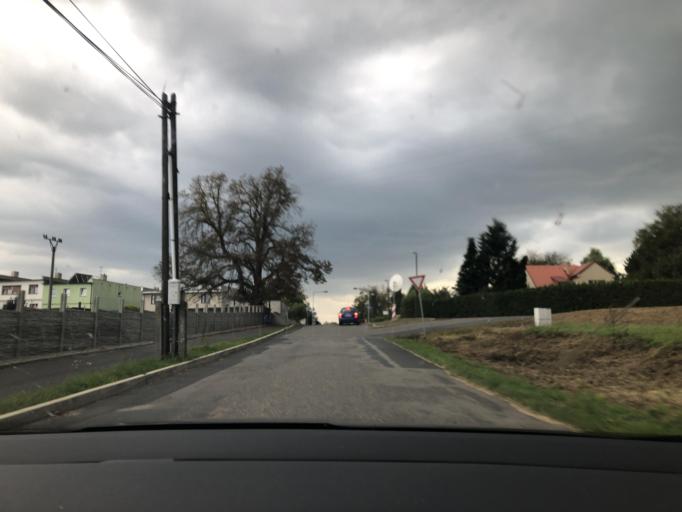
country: CZ
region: Central Bohemia
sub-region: Okres Kolin
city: Tynec nad Labem
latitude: 50.0474
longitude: 15.3642
